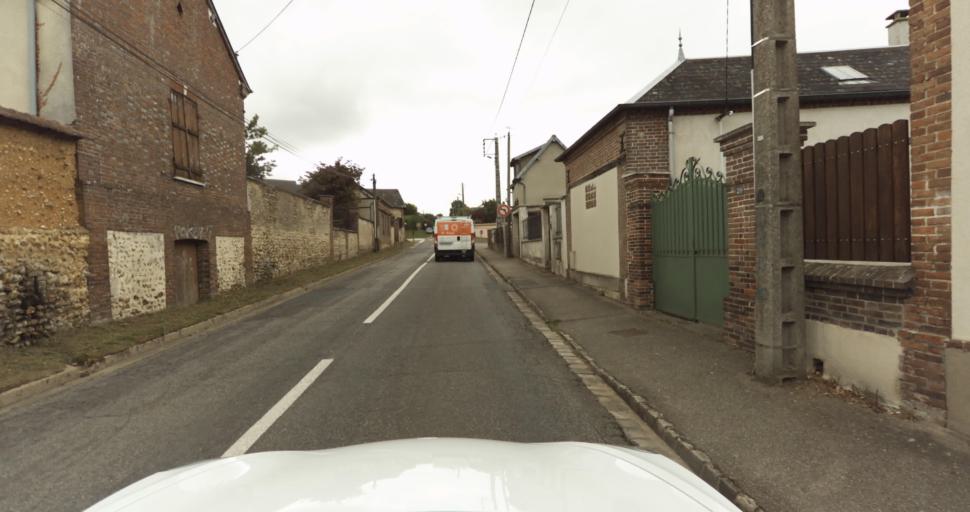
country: FR
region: Haute-Normandie
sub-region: Departement de l'Eure
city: Arnieres-sur-Iton
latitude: 48.9951
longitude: 1.1061
